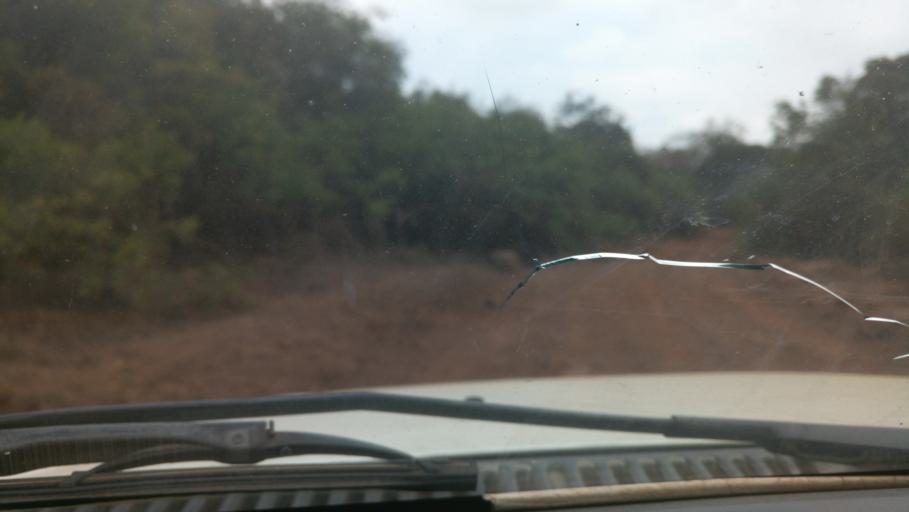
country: KE
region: Nairobi Area
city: Nairobi
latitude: -1.3520
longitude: 36.7671
